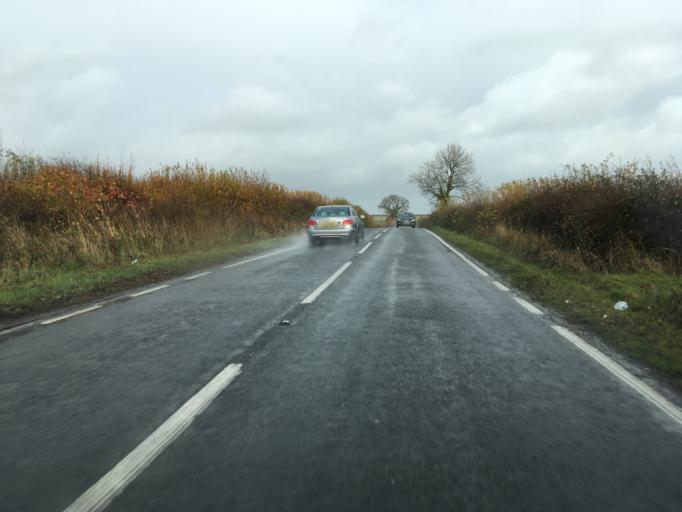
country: GB
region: England
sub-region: South Gloucestershire
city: Cold Ashton
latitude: 51.4611
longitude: -2.3760
